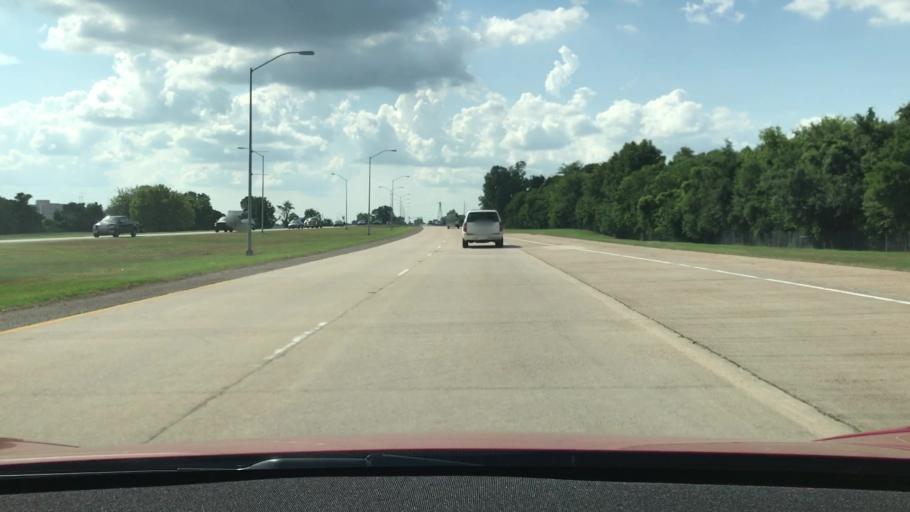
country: US
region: Louisiana
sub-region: Bossier Parish
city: Bossier City
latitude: 32.4969
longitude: -93.6992
